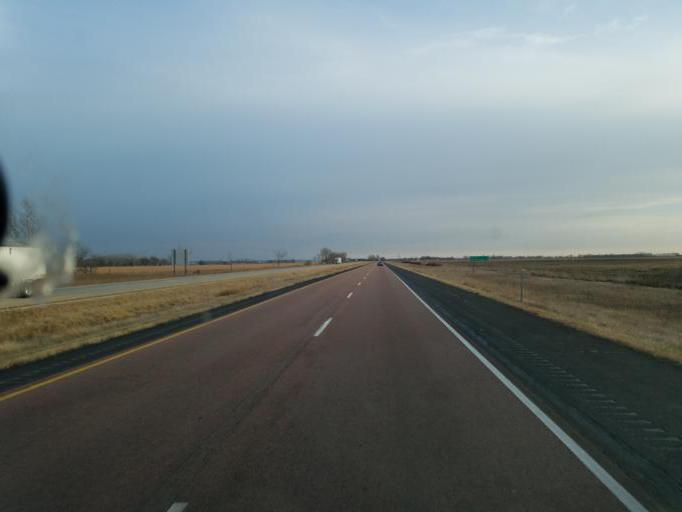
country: US
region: Iowa
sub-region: Monona County
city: Onawa
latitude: 42.0161
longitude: -96.1237
